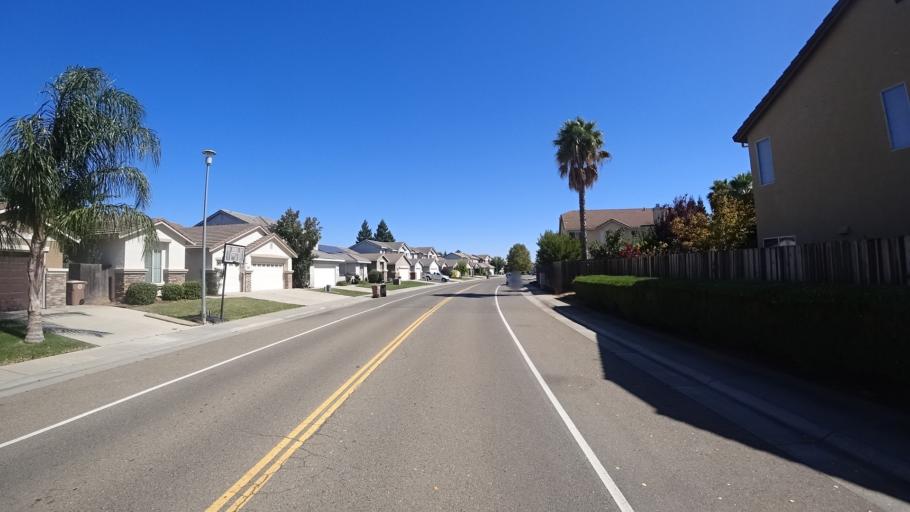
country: US
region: California
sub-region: Sacramento County
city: Elk Grove
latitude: 38.4187
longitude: -121.3413
